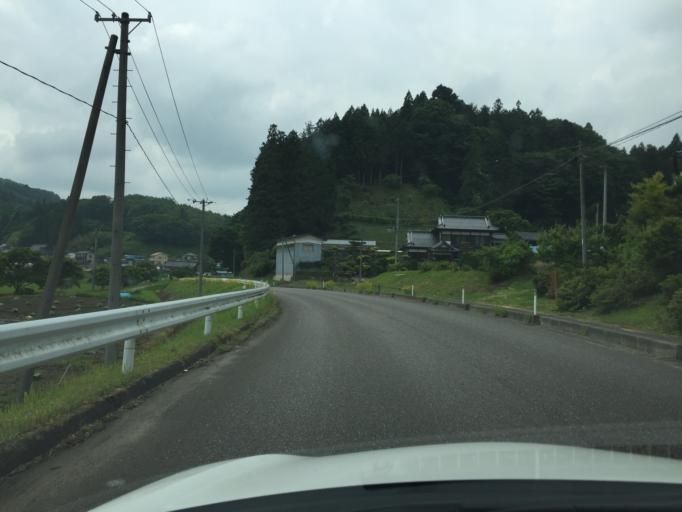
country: JP
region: Fukushima
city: Funehikimachi-funehiki
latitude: 37.2943
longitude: 140.5804
